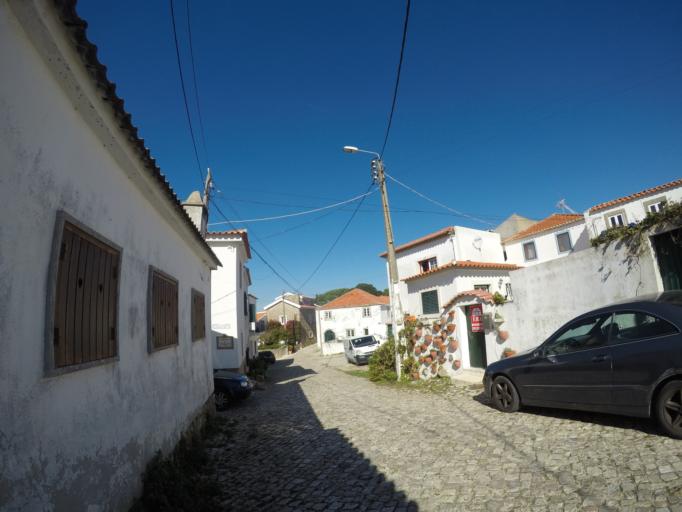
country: PT
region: Lisbon
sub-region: Sintra
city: Colares
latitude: 38.7864
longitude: -9.4760
